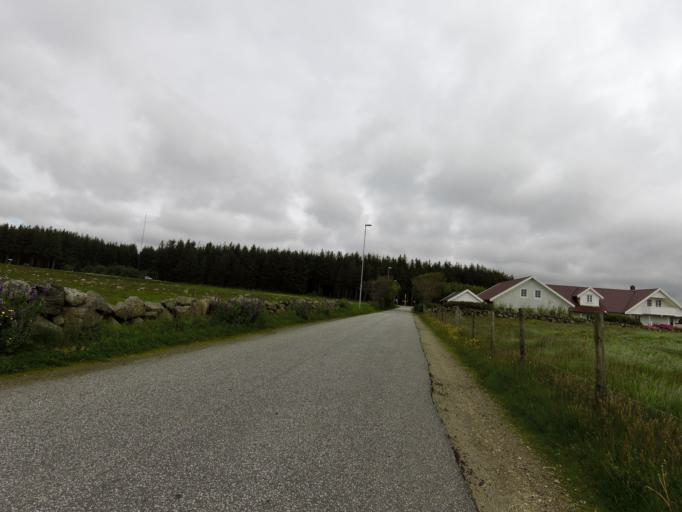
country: NO
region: Rogaland
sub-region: Ha
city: Naerbo
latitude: 58.6529
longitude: 5.5973
